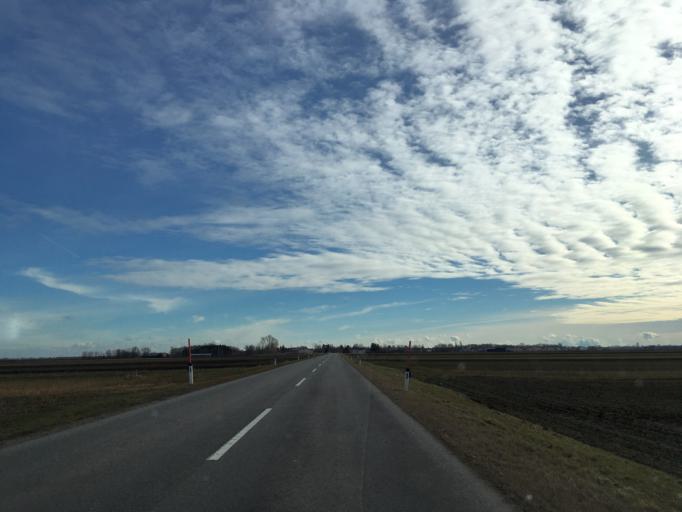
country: AT
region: Burgenland
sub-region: Politischer Bezirk Neusiedl am See
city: Pama
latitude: 48.0578
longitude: 17.0175
